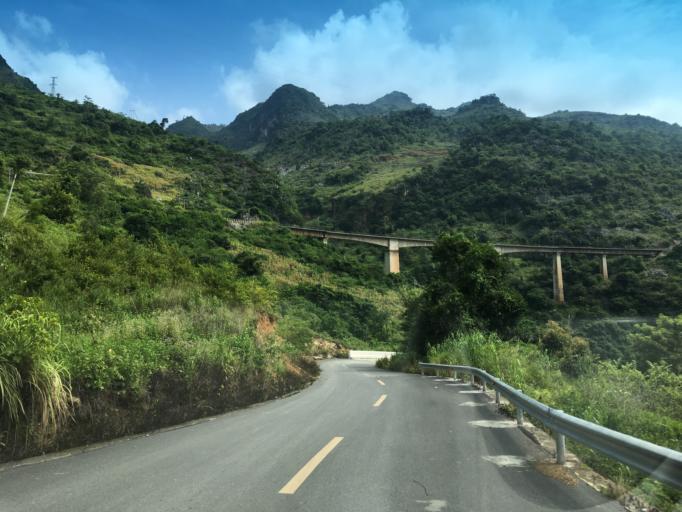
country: CN
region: Guangxi Zhuangzu Zizhiqu
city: Xinzhou
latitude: 24.8195
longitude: 105.6485
